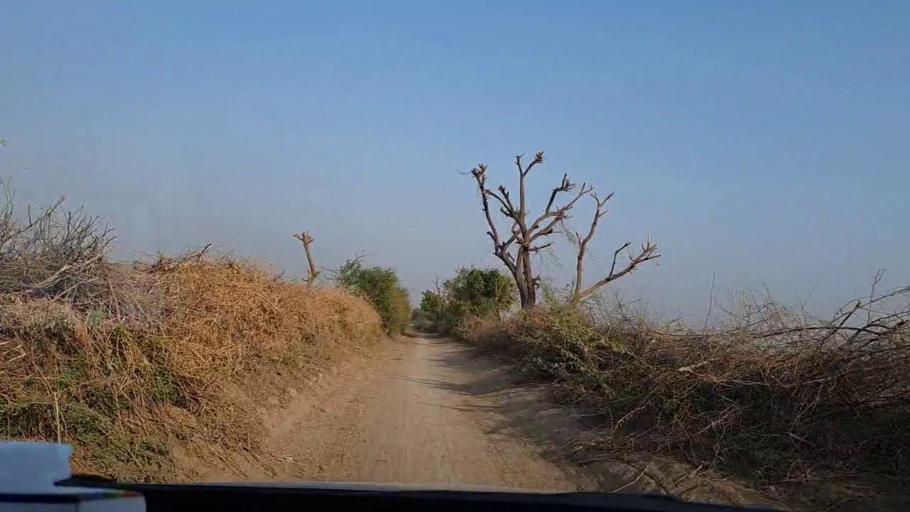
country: PK
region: Sindh
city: Tando Ghulam Ali
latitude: 25.2096
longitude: 68.9122
